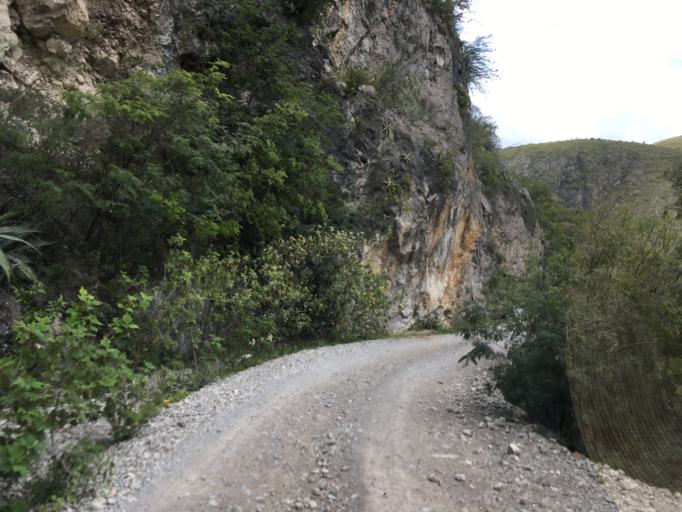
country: MX
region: Hidalgo
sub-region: Metztitlan
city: Fontezuelas
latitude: 20.6273
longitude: -98.8912
